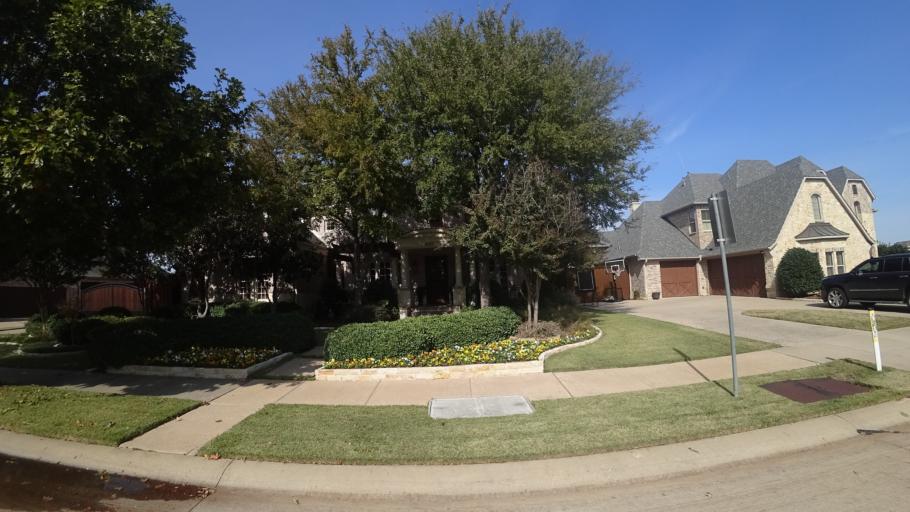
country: US
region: Texas
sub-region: Denton County
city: The Colony
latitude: 33.0371
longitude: -96.8920
